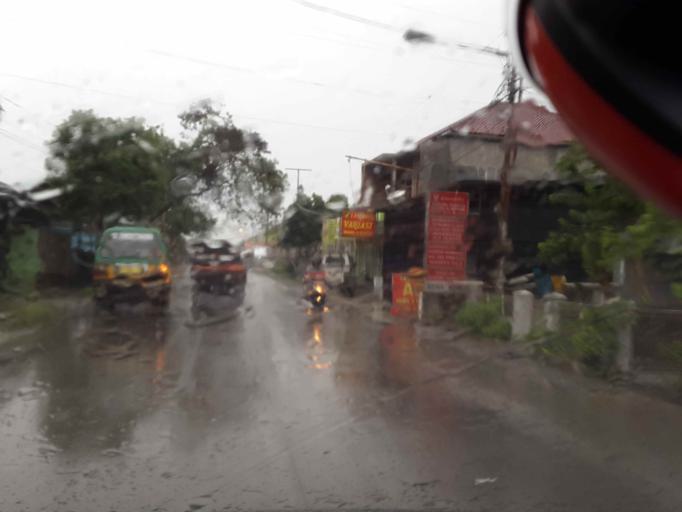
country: ID
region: West Java
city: Cimahi
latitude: -6.9266
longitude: 107.4990
